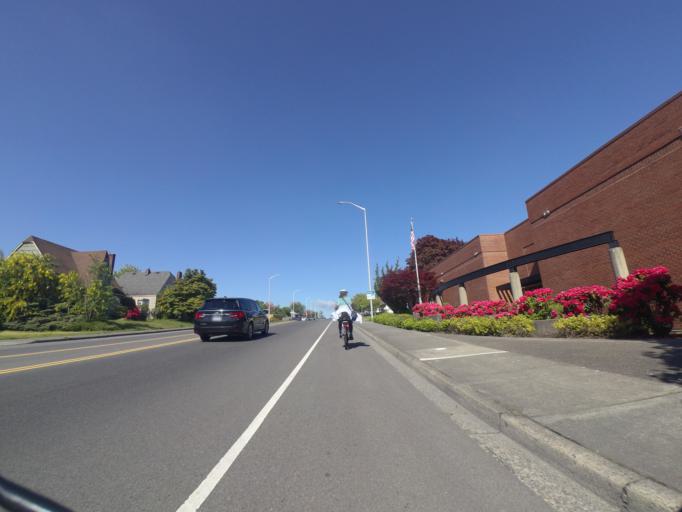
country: US
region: Washington
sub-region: Pierce County
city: Tacoma
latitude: 47.2065
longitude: -122.4355
